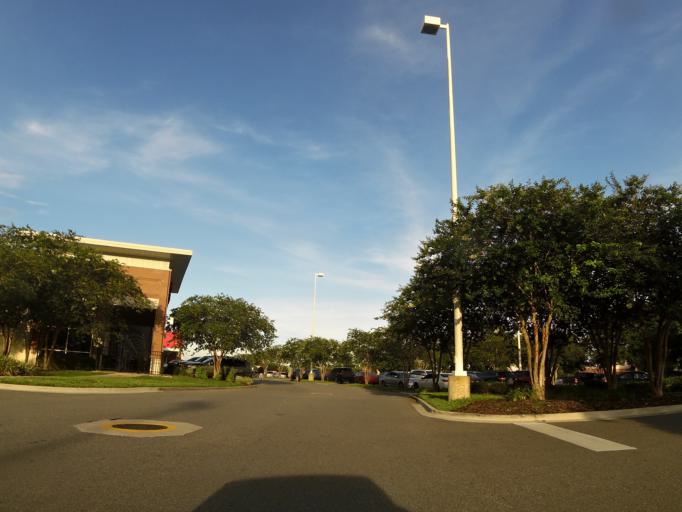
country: US
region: Florida
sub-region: Saint Johns County
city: Ponte Vedra Beach
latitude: 30.2173
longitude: -81.5197
